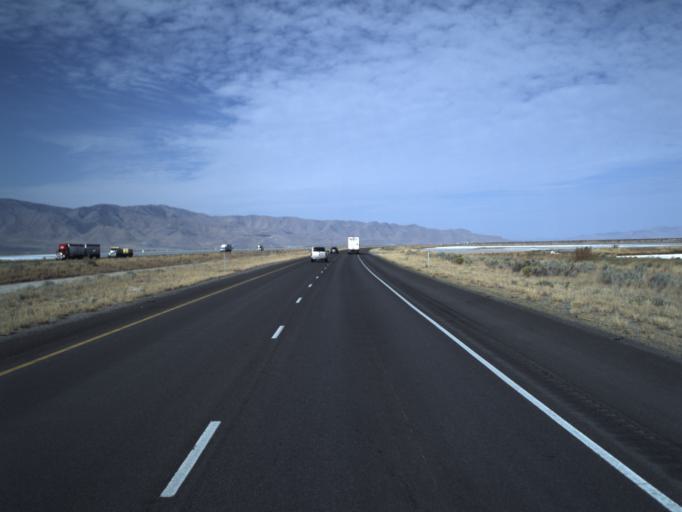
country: US
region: Utah
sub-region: Tooele County
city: Stansbury park
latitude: 40.6633
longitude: -112.3538
